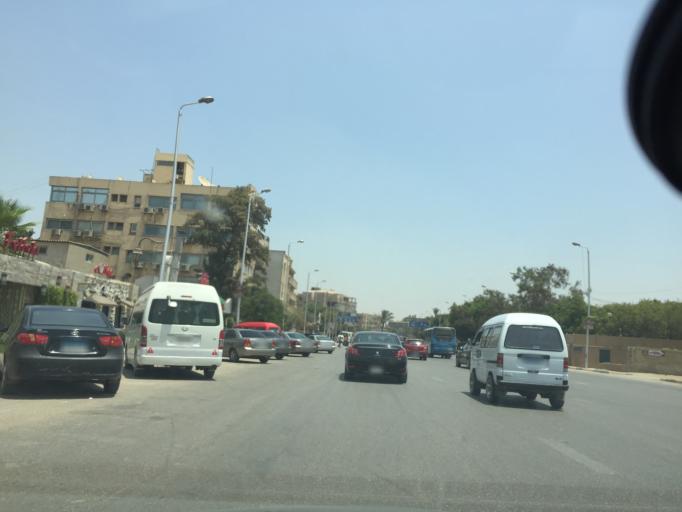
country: EG
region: Al Jizah
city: Al Jizah
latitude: 29.9879
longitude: 31.1311
